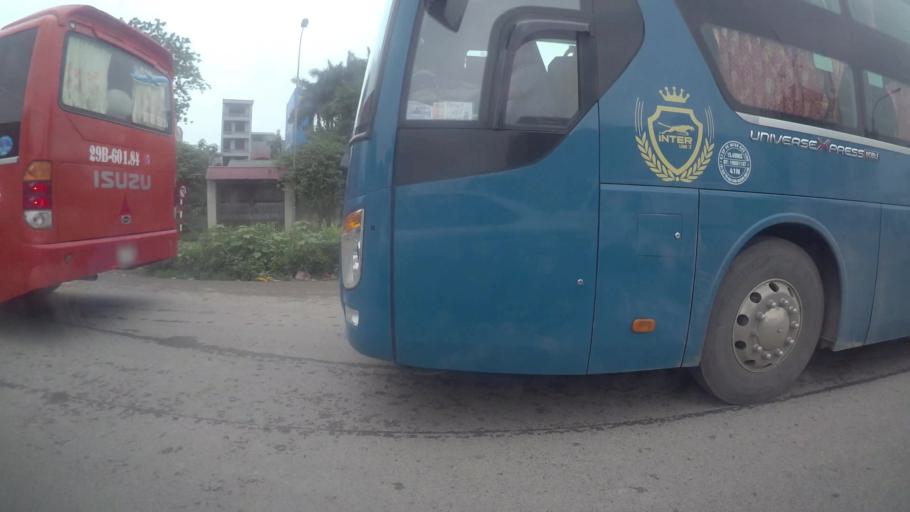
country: VN
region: Ha Noi
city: Tay Ho
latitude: 21.0806
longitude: 105.7881
